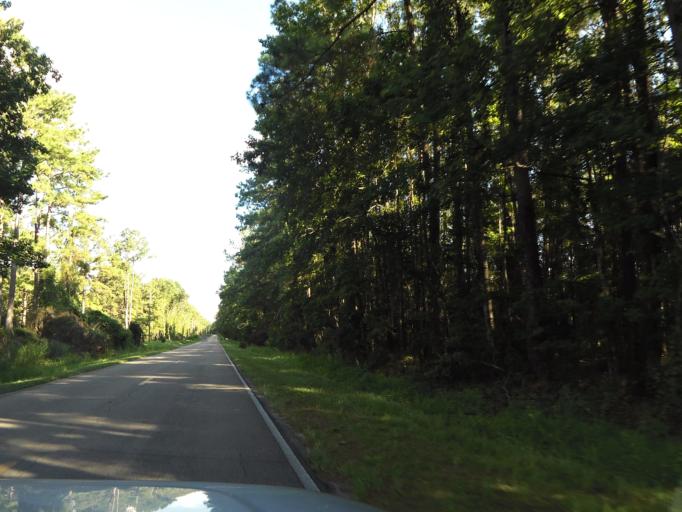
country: US
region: Florida
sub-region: Wakulla County
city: Crawfordville
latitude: 30.0688
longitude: -84.5060
